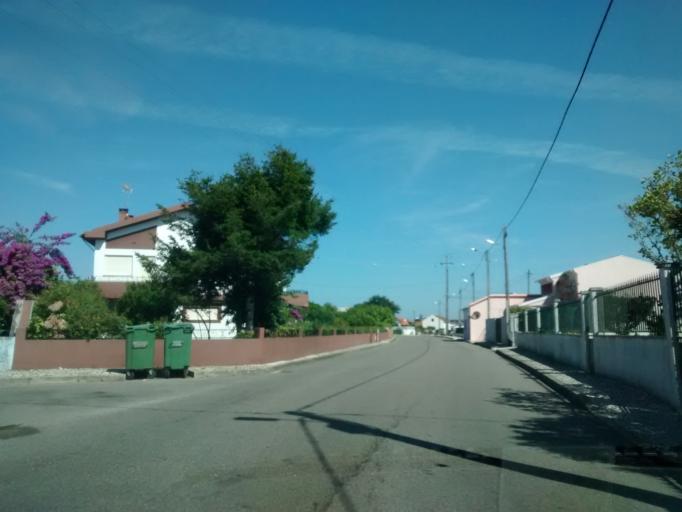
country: PT
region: Coimbra
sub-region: Mira
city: Mira
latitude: 40.4355
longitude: -8.7131
